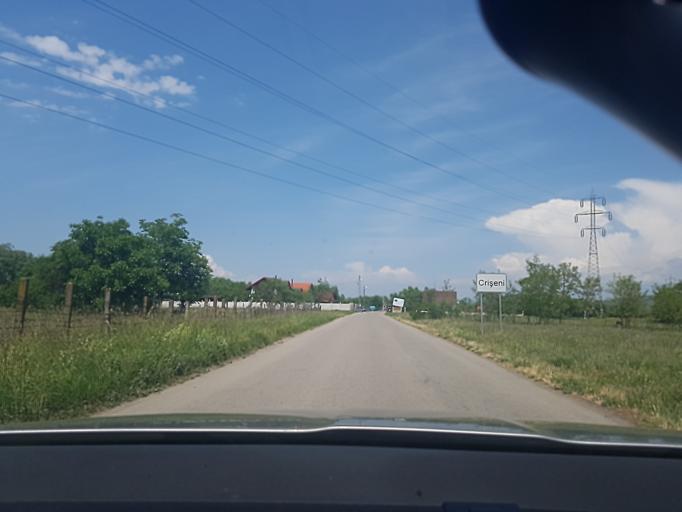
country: RO
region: Hunedoara
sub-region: Comuna Calan
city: Calan
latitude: 45.7360
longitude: 23.0092
